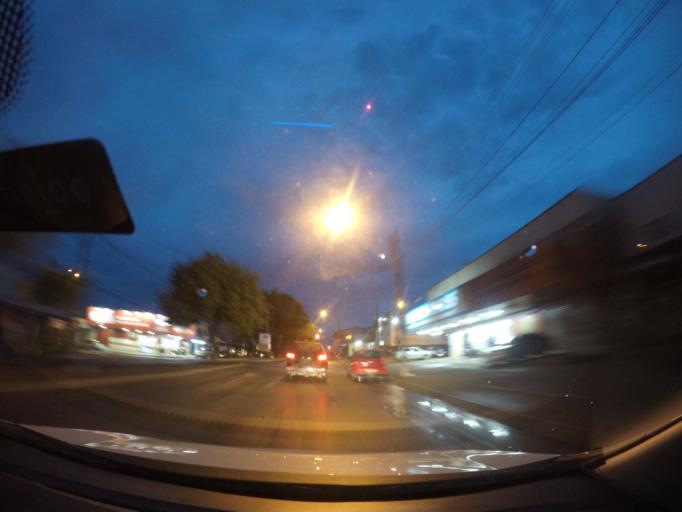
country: BR
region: Goias
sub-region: Goiania
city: Goiania
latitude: -16.7237
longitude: -49.3732
